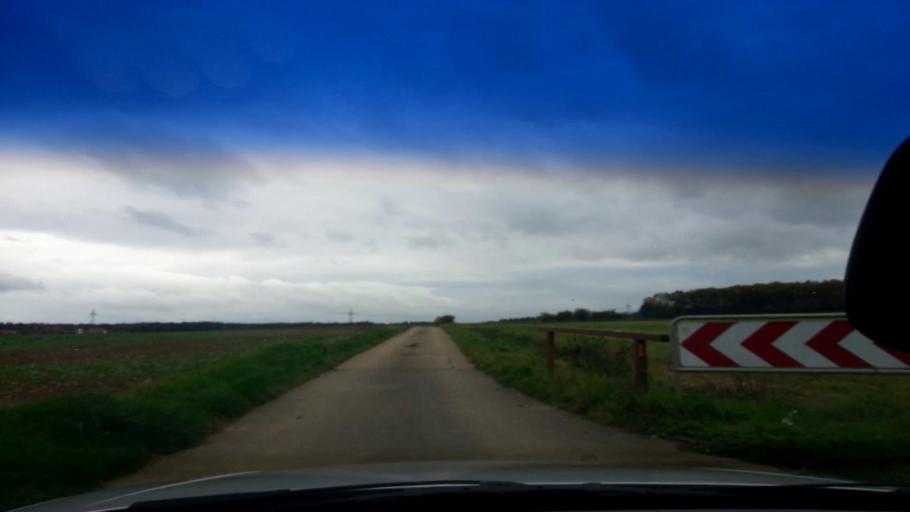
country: DE
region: Bavaria
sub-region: Upper Franconia
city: Memmelsdorf
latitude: 49.9621
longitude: 10.9530
